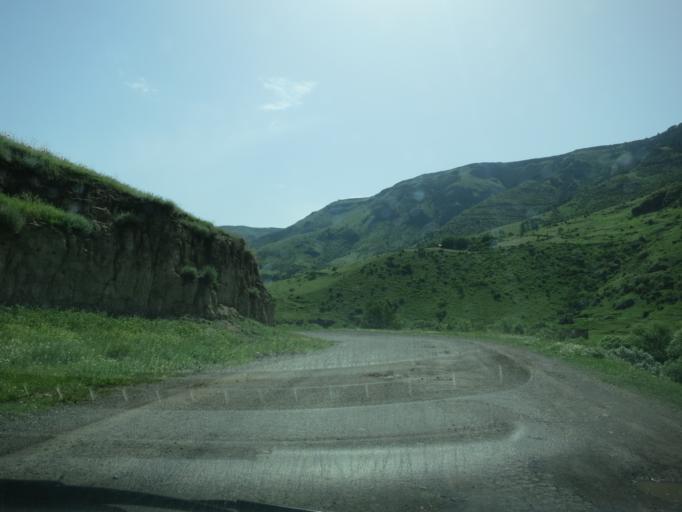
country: TR
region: Ardahan
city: Kurtkale
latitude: 41.3756
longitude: 43.2743
